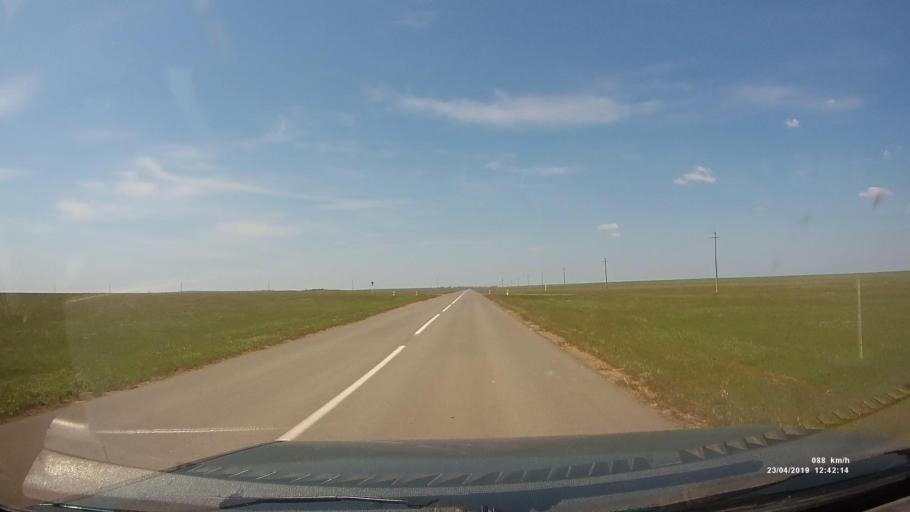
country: RU
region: Kalmykiya
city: Yashalta
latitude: 46.4544
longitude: 42.6686
